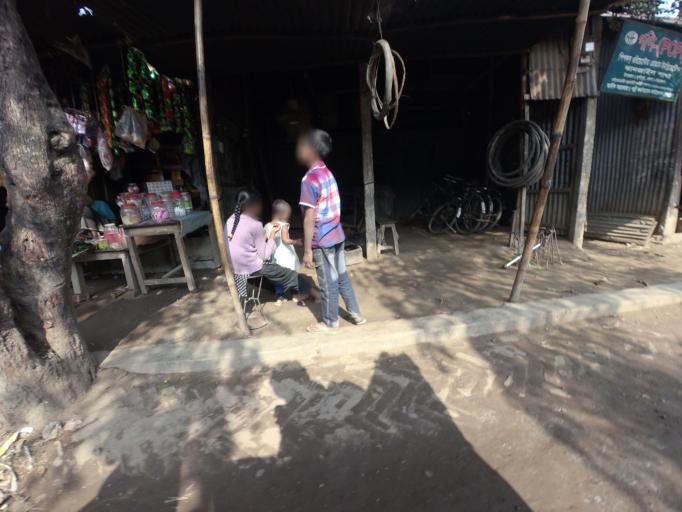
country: BD
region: Dhaka
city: Netrakona
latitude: 25.0138
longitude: 90.6481
